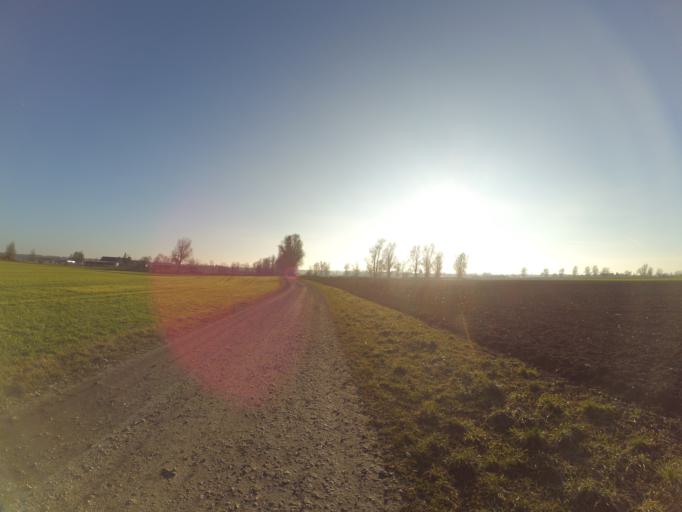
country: DE
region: Bavaria
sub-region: Swabia
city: Leipheim
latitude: 48.4717
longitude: 10.2082
